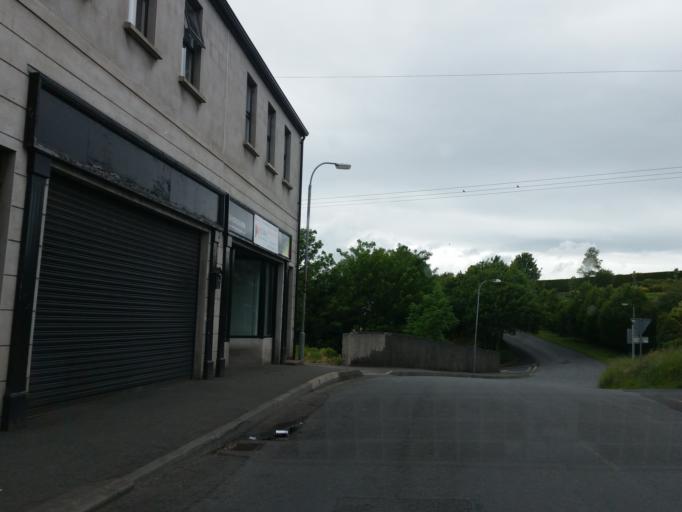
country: IE
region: Ulster
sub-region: County Monaghan
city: Monaghan
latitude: 54.4631
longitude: -7.0282
